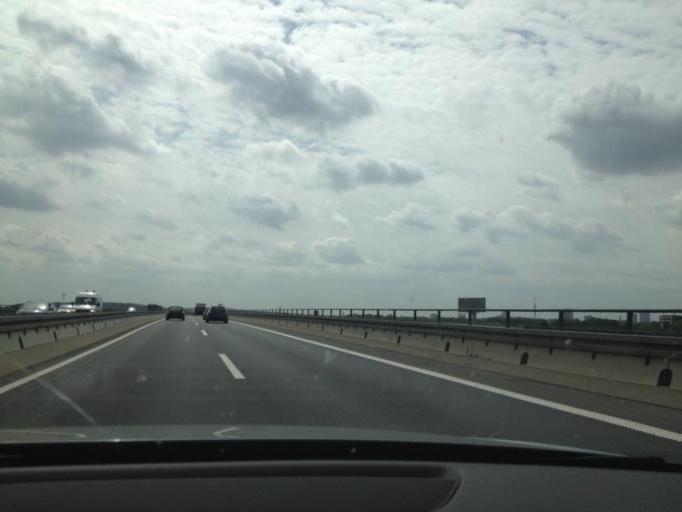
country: DE
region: North Rhine-Westphalia
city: Meiderich
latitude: 51.4572
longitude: 6.7753
